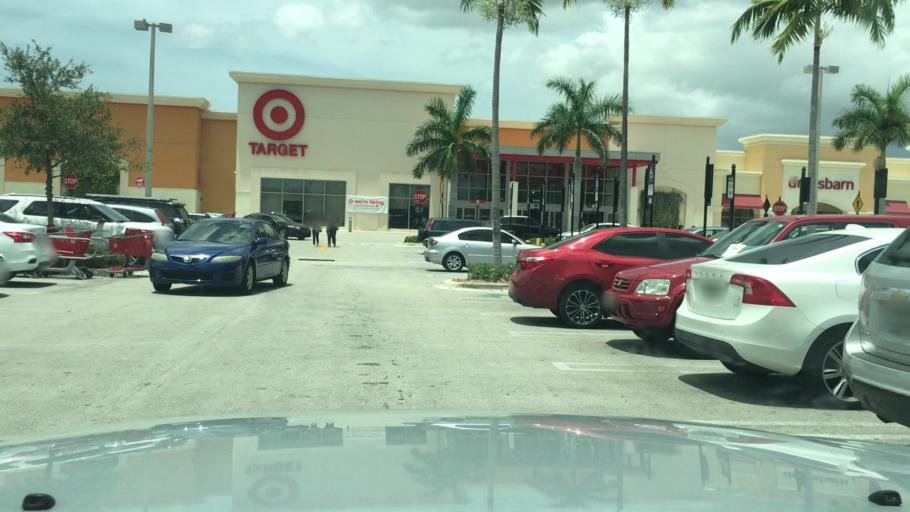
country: US
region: Florida
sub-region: Miami-Dade County
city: Fountainebleau
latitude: 25.7706
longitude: -80.3599
